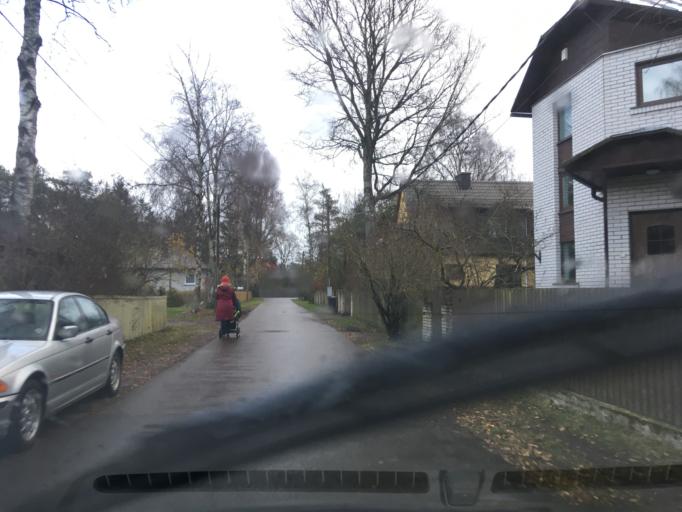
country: EE
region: Harju
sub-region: Tallinna linn
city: Tallinn
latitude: 59.3734
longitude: 24.7122
